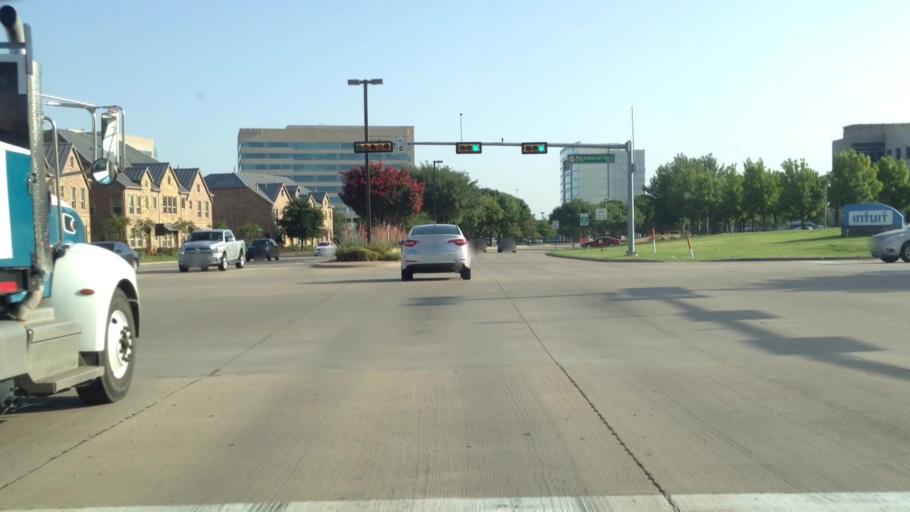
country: US
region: Texas
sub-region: Collin County
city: Frisco
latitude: 33.0839
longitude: -96.8185
